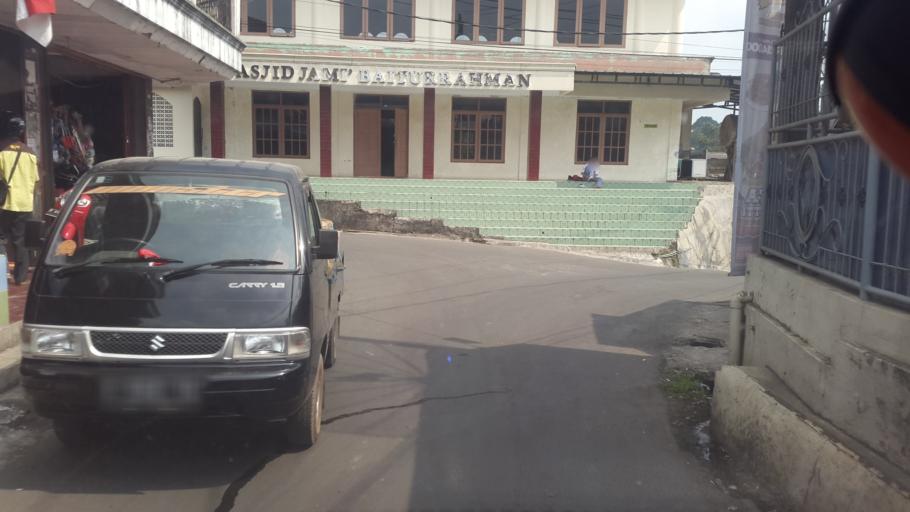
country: ID
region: West Java
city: Cicurug
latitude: -6.7641
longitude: 106.7654
